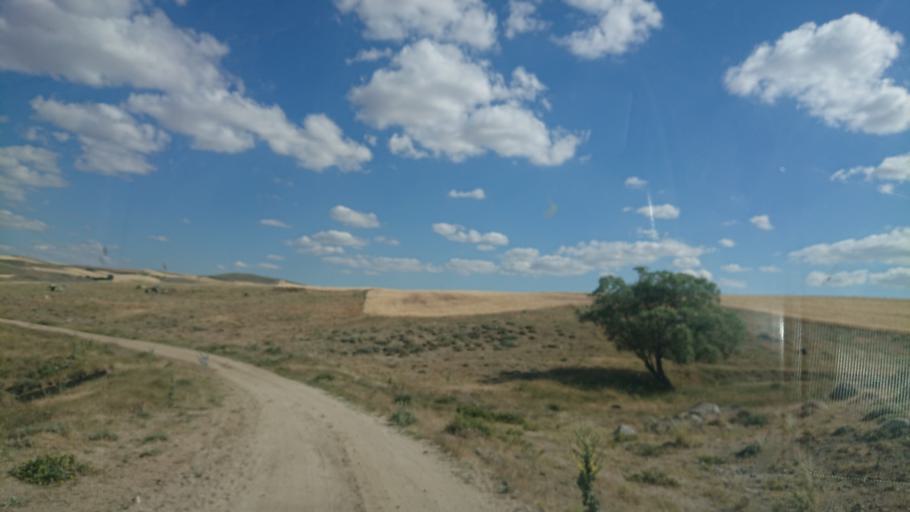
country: TR
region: Aksaray
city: Sariyahsi
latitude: 38.9202
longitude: 33.8524
